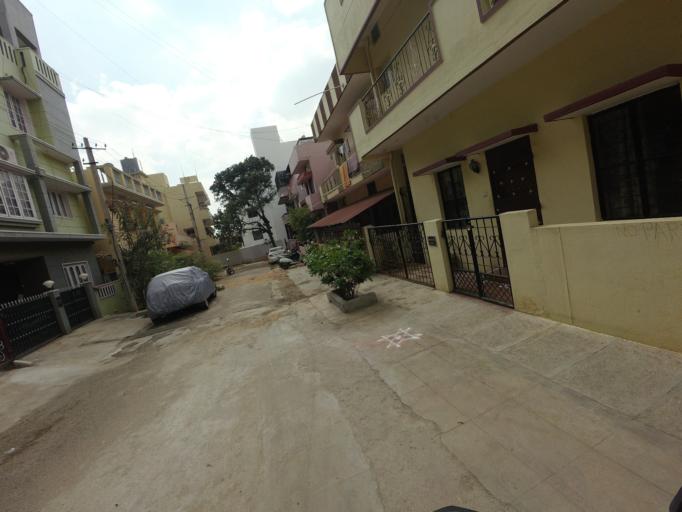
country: IN
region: Karnataka
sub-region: Bangalore Urban
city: Bangalore
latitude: 12.9628
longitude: 77.5346
